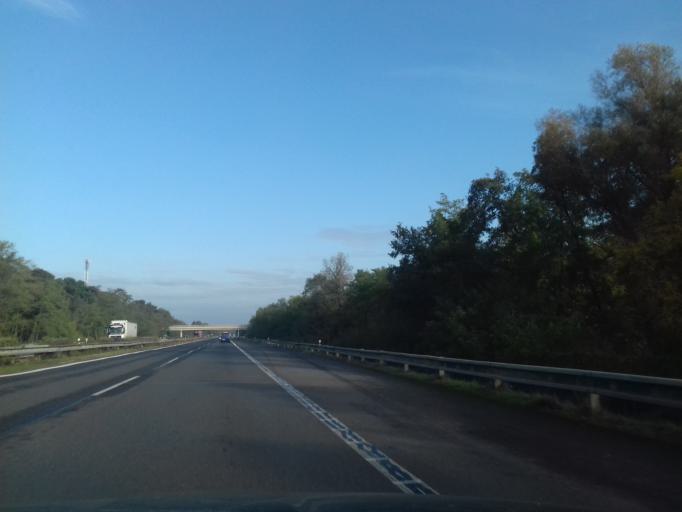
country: SK
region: Bratislavsky
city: Stupava
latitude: 48.3448
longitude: 17.0226
